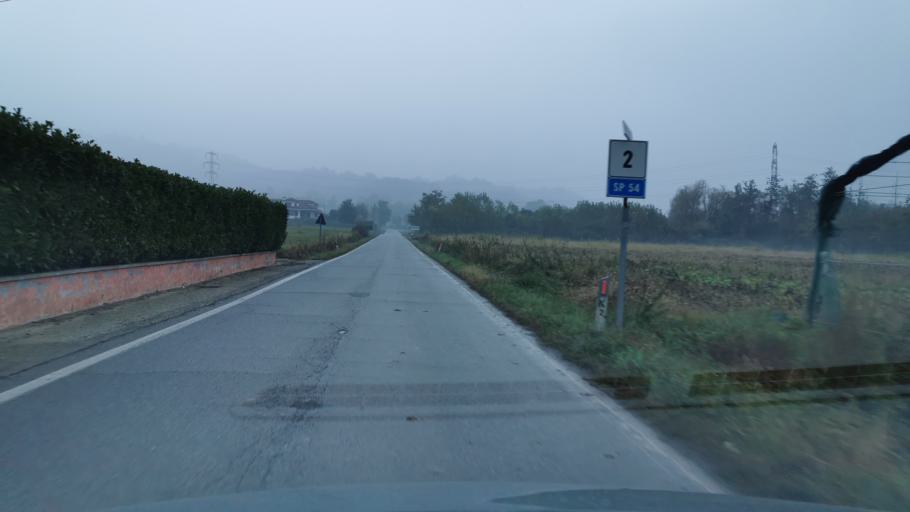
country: IT
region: Piedmont
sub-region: Provincia di Torino
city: Aglie
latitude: 45.3673
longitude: 7.7871
